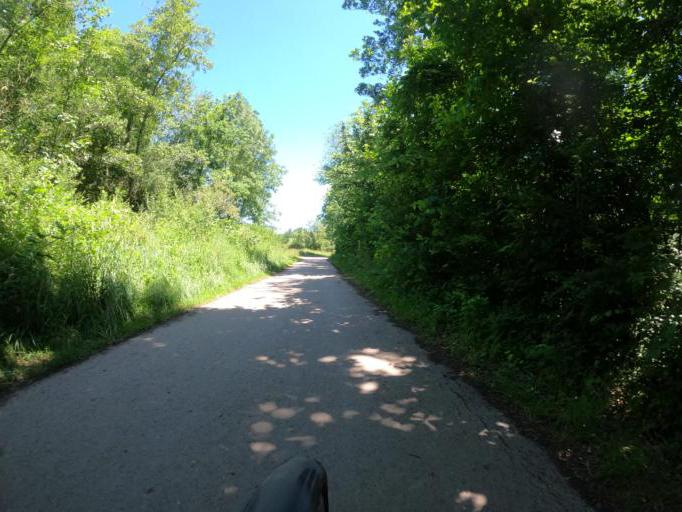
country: DE
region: Baden-Wuerttemberg
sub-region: Regierungsbezirk Stuttgart
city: Vaihingen an der Enz
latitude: 48.9636
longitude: 8.9663
